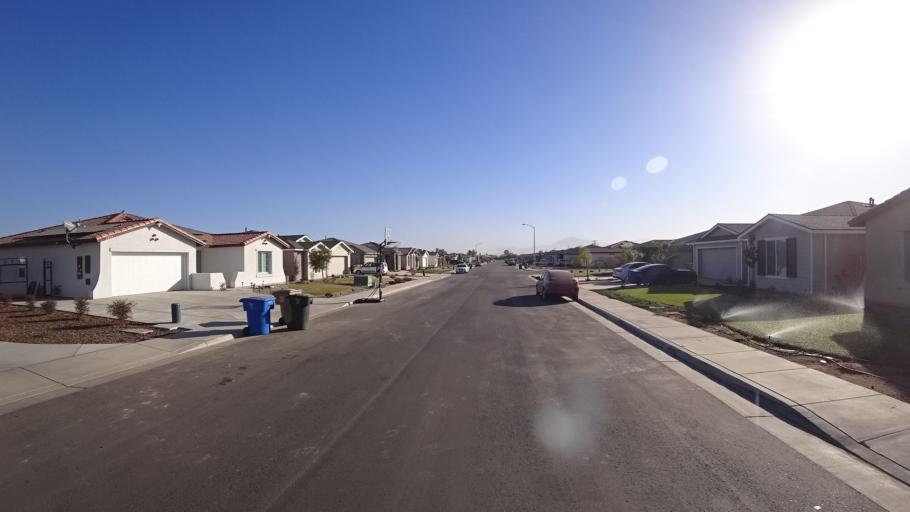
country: US
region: California
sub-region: Kern County
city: Greenfield
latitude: 35.2710
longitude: -119.0337
